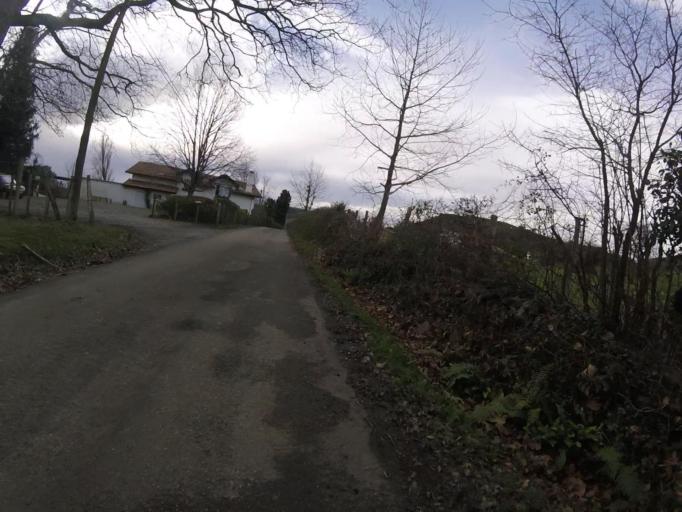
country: FR
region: Aquitaine
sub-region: Departement des Pyrenees-Atlantiques
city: Urrugne
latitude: 43.3404
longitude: -1.6990
